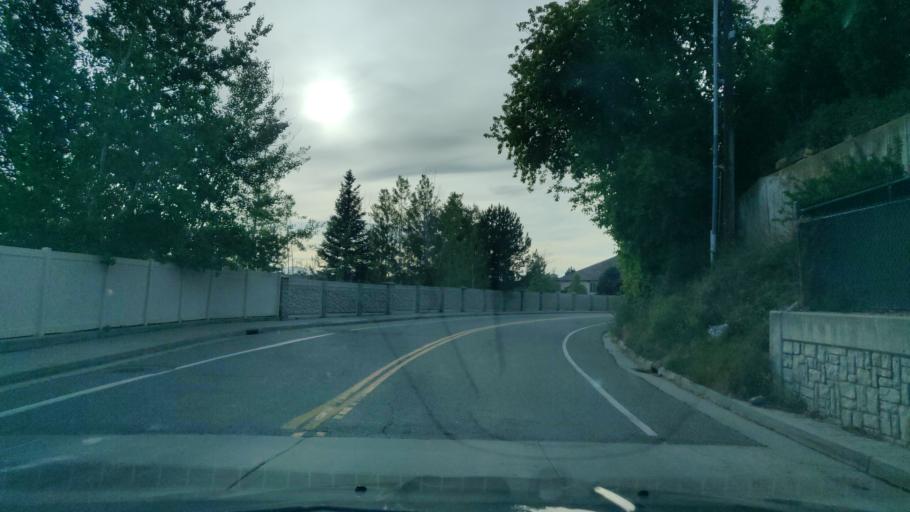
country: US
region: Utah
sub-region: Salt Lake County
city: Cottonwood Heights
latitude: 40.6058
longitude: -111.8075
